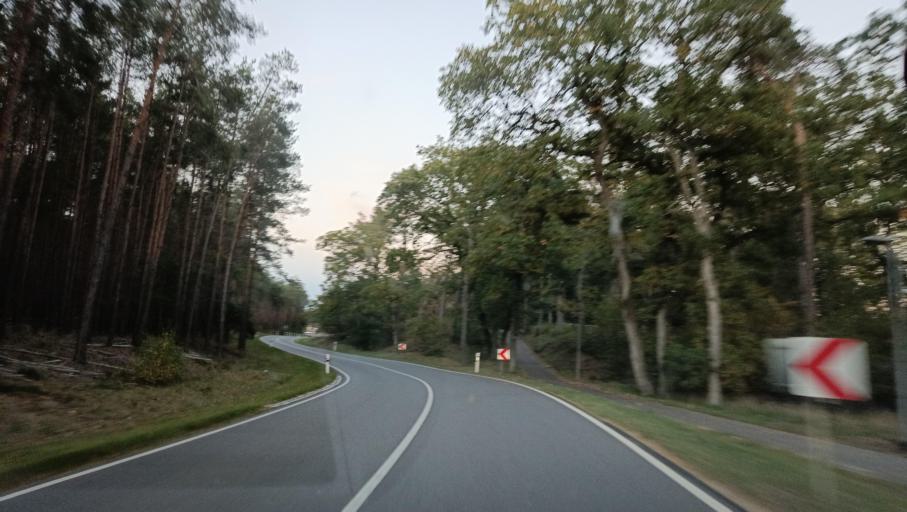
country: DE
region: Mecklenburg-Vorpommern
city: Grabow
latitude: 53.2784
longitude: 11.5480
